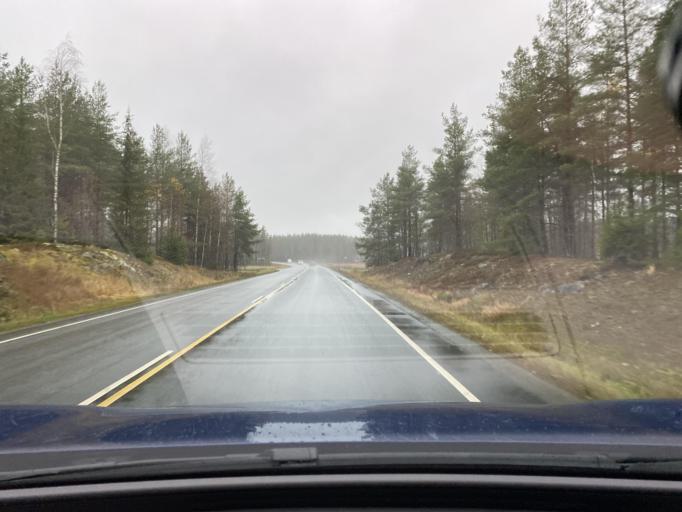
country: FI
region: Varsinais-Suomi
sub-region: Loimaa
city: Alastaro
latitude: 60.9230
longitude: 22.8929
